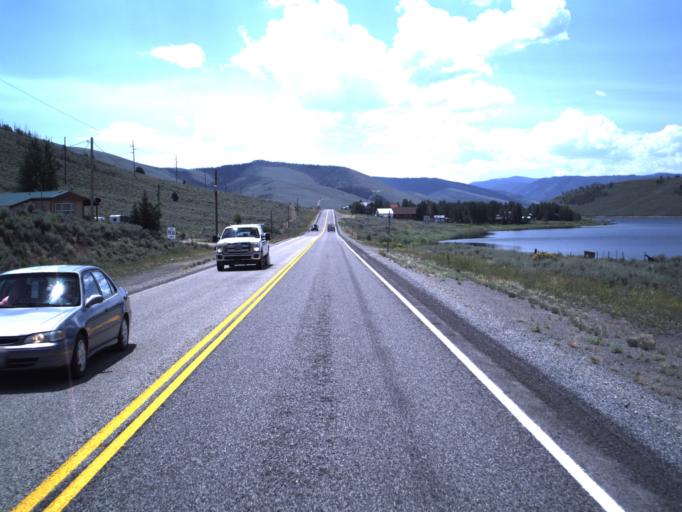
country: US
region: Utah
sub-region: Carbon County
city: Helper
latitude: 39.8114
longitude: -111.1352
